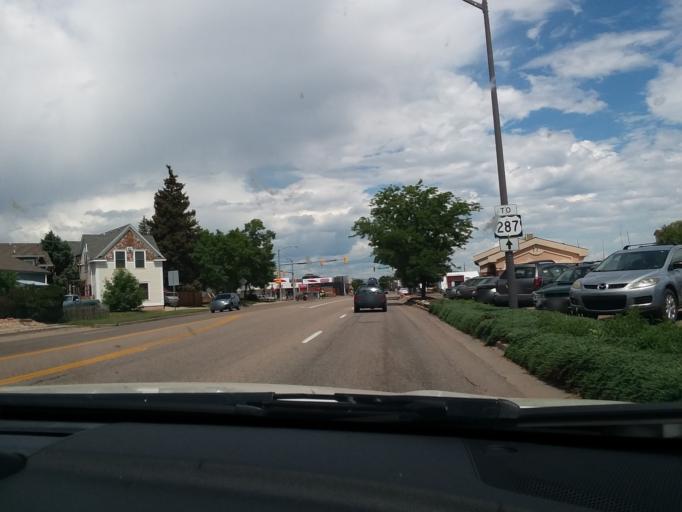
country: US
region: Colorado
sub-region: Larimer County
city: Fort Collins
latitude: 40.5865
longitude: -105.0706
